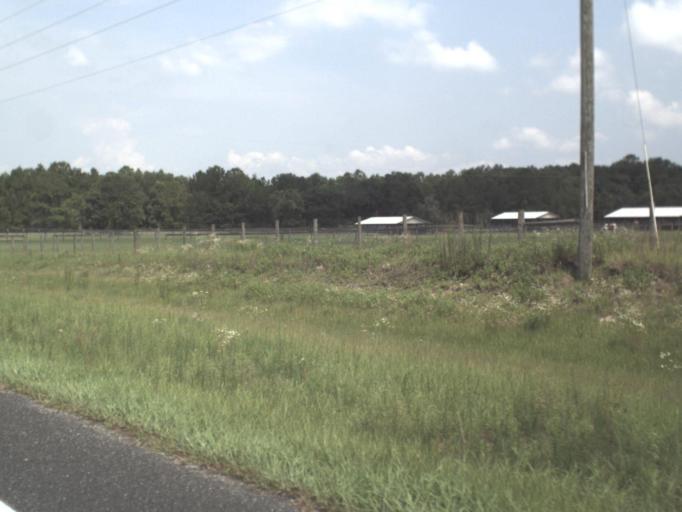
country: US
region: Florida
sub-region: Levy County
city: Bronson
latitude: 29.4758
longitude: -82.7331
